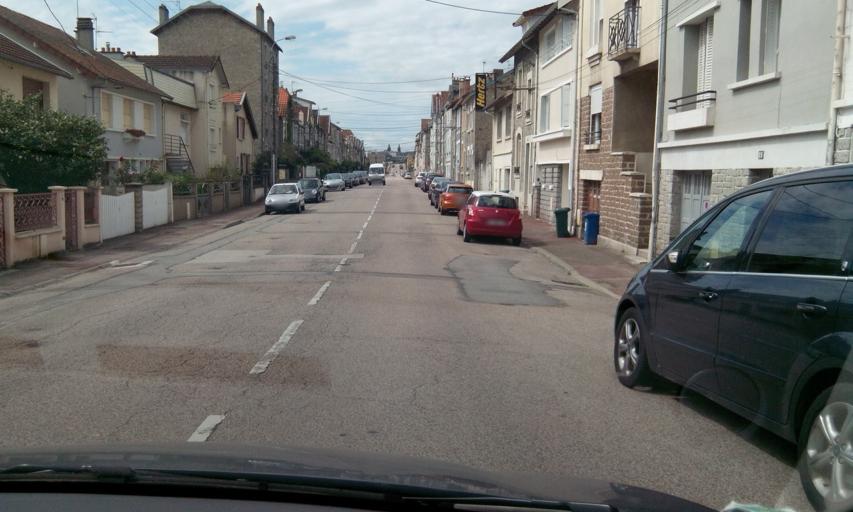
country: FR
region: Limousin
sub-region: Departement de la Haute-Vienne
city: Limoges
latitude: 45.8390
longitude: 1.2736
